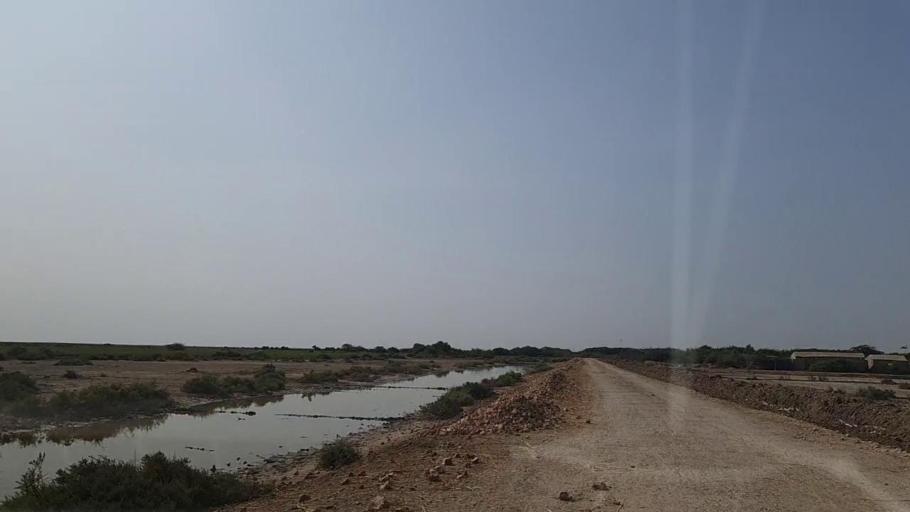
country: PK
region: Sindh
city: Chuhar Jamali
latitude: 24.2006
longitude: 67.8227
